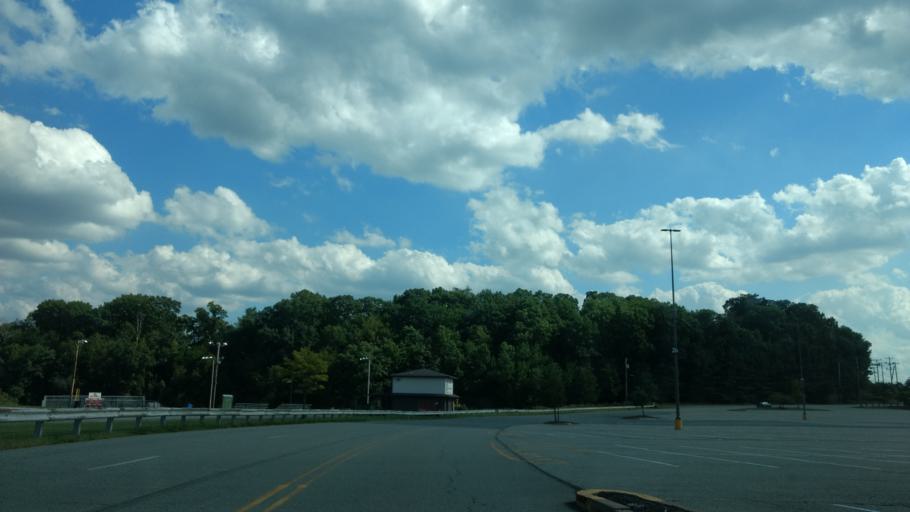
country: US
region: Pennsylvania
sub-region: Allegheny County
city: West View
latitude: 40.5451
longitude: -80.0047
